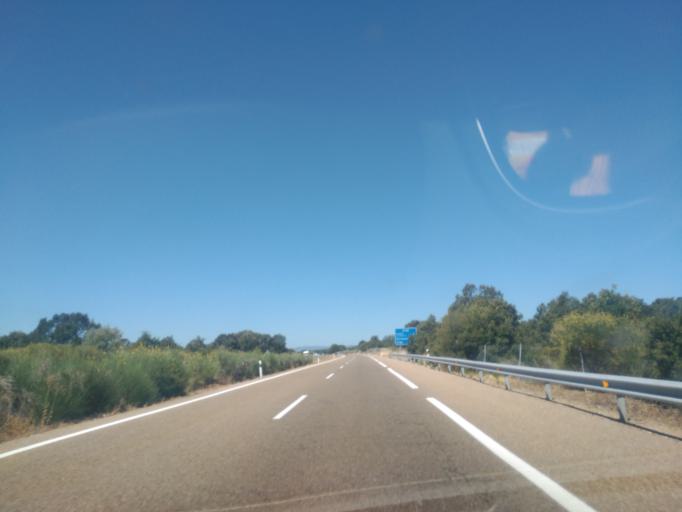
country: ES
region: Castille and Leon
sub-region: Provincia de Zamora
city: Mombuey
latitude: 42.0172
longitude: -6.3148
